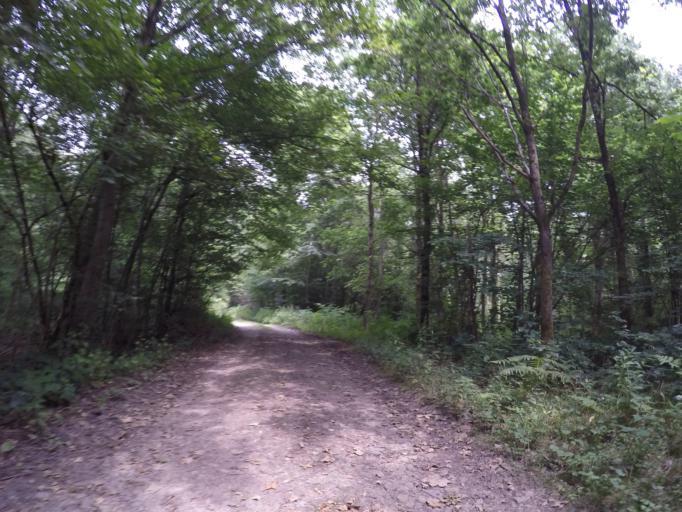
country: BE
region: Wallonia
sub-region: Province de Namur
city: Yvoir
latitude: 50.3335
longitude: 4.9489
